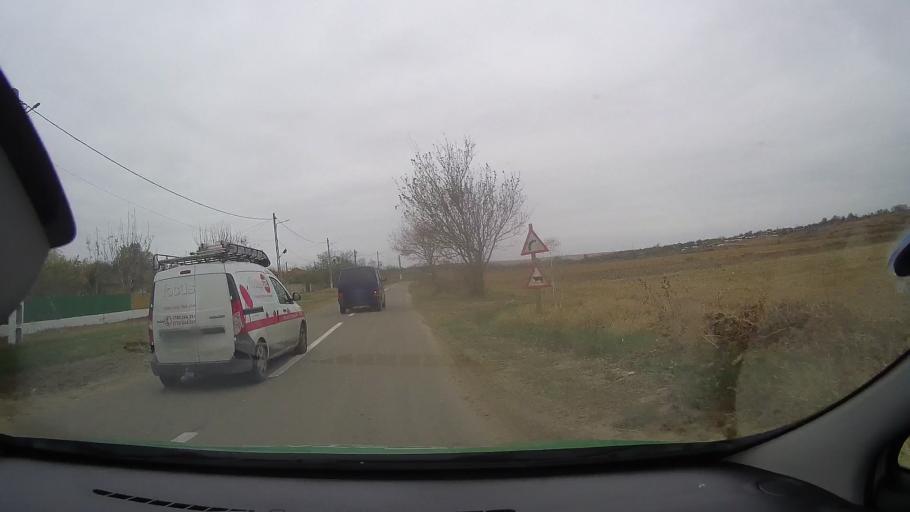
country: RO
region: Constanta
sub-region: Comuna Saraiu
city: Saraiu
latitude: 44.7236
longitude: 28.1681
